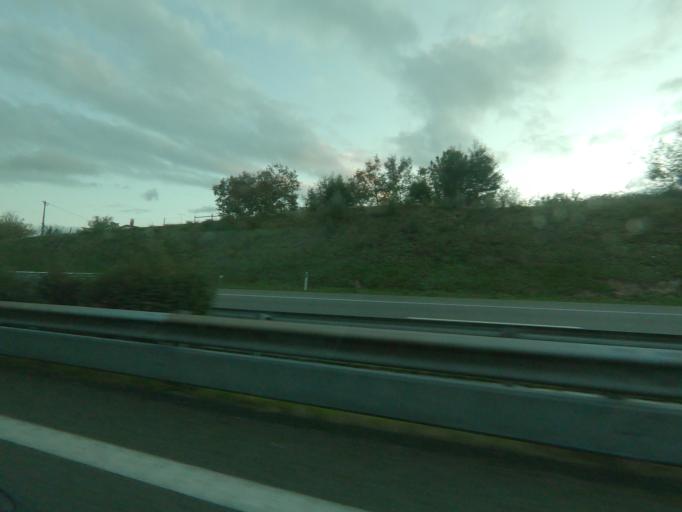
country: PT
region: Porto
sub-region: Marco de Canaveses
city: Marco de Canavezes
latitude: 41.2218
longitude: -8.1664
